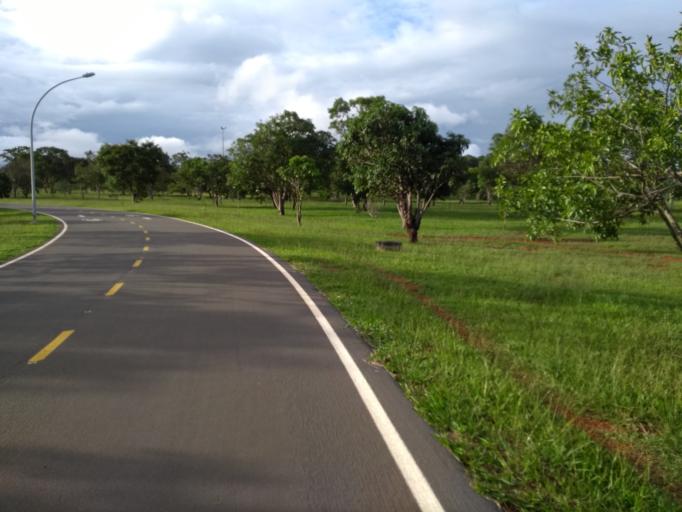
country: BR
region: Federal District
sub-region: Brasilia
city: Brasilia
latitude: -15.8110
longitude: -47.9228
